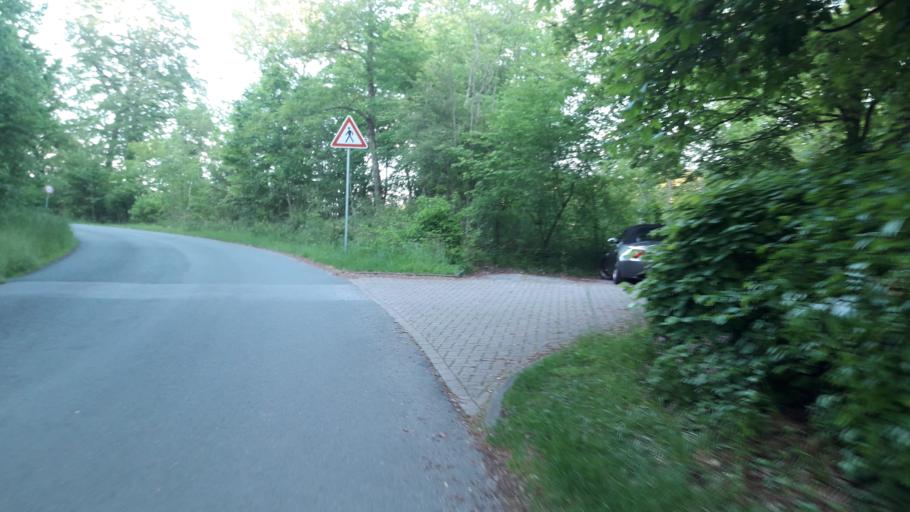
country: DE
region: North Rhine-Westphalia
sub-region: Regierungsbezirk Detmold
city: Paderborn
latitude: 51.6641
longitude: 8.7695
